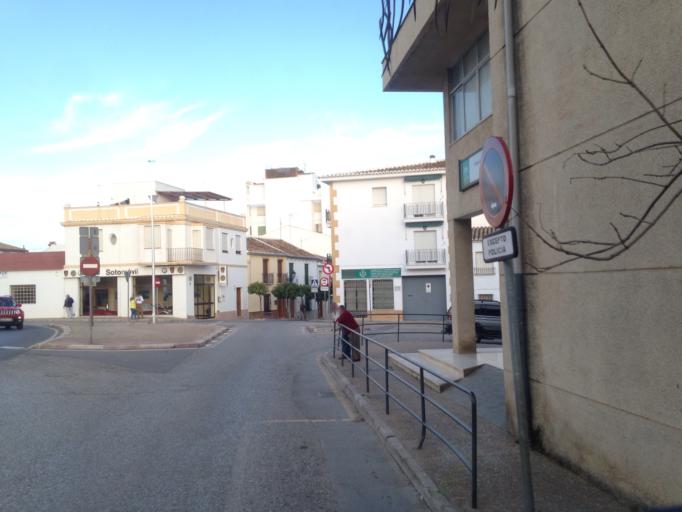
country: ES
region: Andalusia
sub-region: Provincia de Malaga
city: Antequera
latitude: 37.0227
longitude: -4.5630
